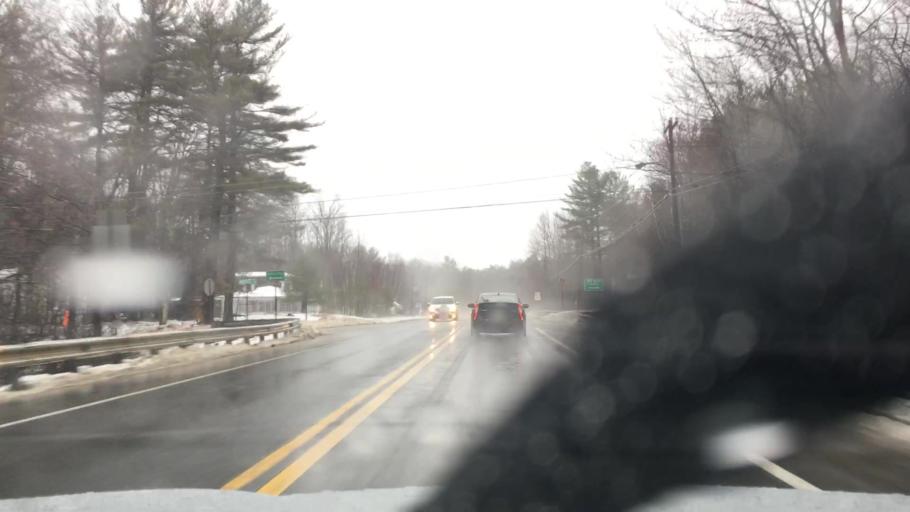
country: US
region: Massachusetts
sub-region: Franklin County
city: Wendell
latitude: 42.5039
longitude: -72.3340
